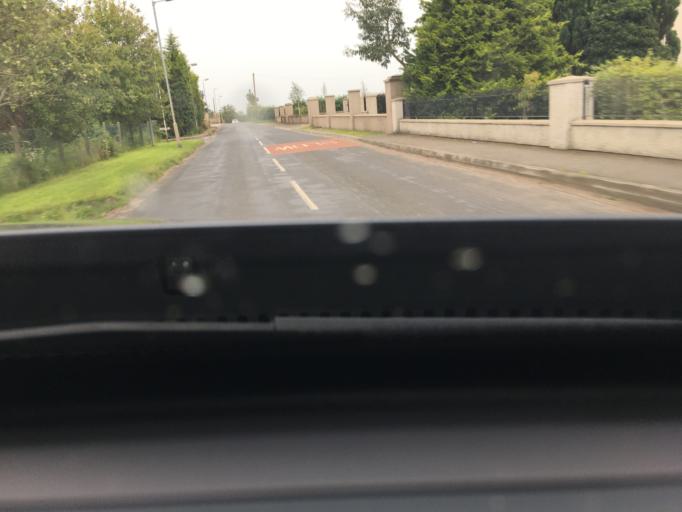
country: GB
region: Northern Ireland
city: Coalisland
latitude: 54.5384
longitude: -6.6213
